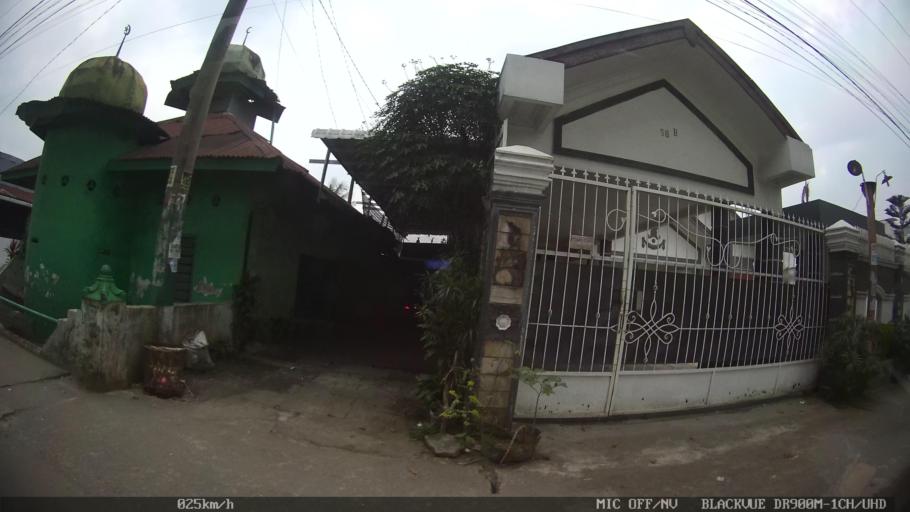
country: ID
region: North Sumatra
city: Deli Tua
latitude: 3.5403
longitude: 98.6985
